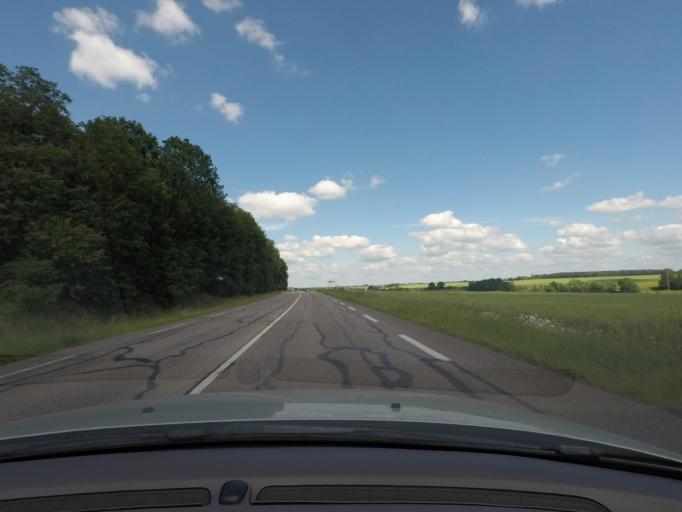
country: FR
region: Haute-Normandie
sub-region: Departement de l'Eure
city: Verneuil-sur-Avre
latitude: 48.7199
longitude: 0.8804
